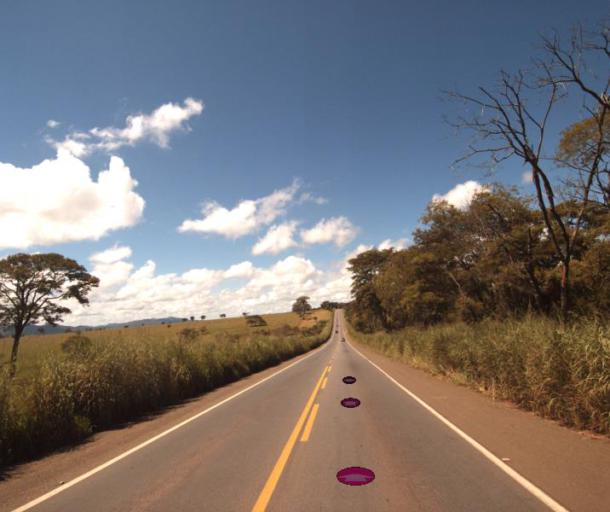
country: BR
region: Goias
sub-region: Jaragua
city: Jaragua
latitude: -15.8301
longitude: -49.2795
